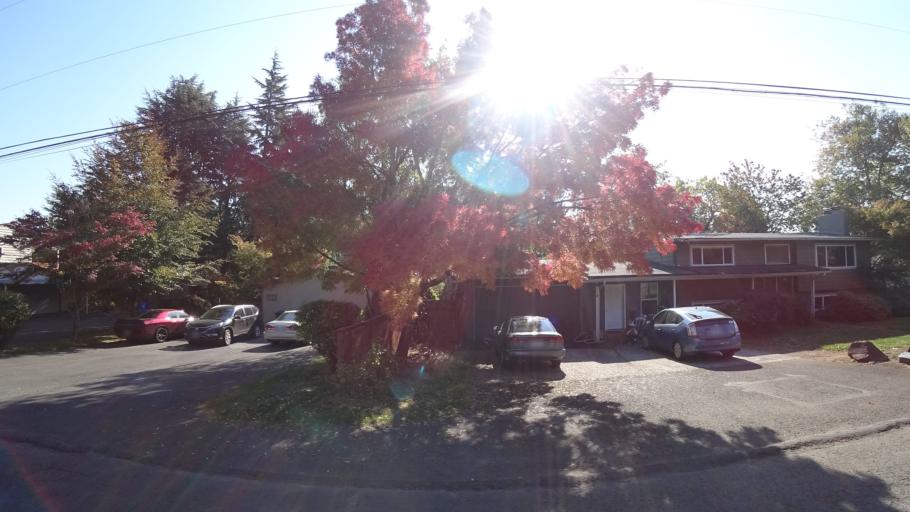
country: US
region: Oregon
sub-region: Multnomah County
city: Gresham
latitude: 45.4988
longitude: -122.4485
